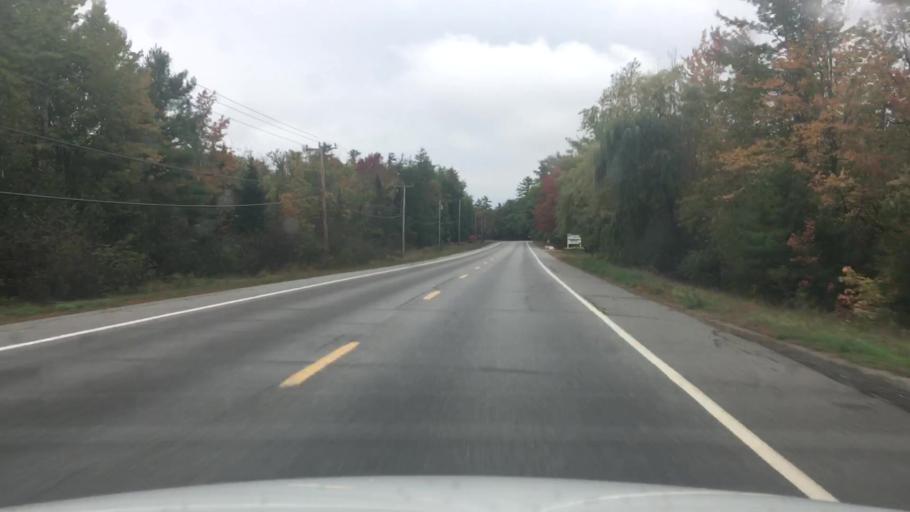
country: US
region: Maine
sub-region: Kennebec County
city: Rome
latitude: 44.5179
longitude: -69.8778
